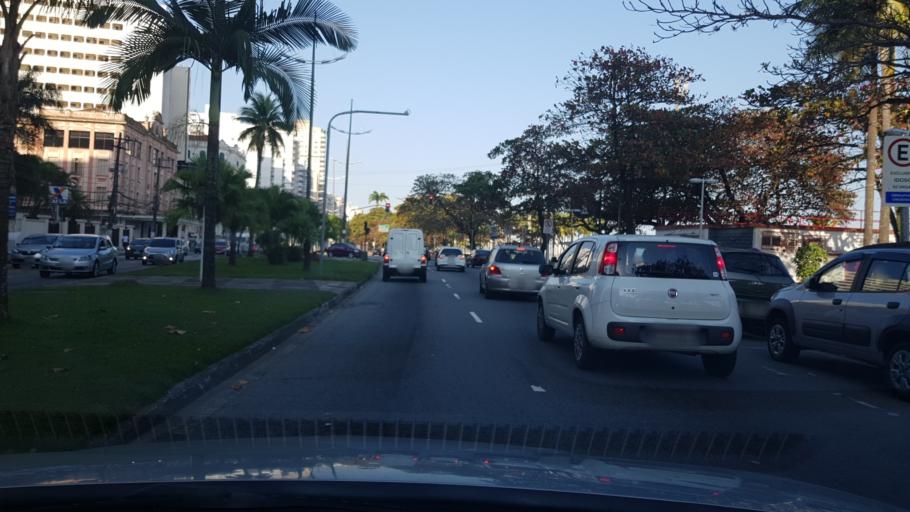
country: BR
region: Sao Paulo
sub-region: Santos
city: Santos
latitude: -23.9691
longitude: -46.3353
